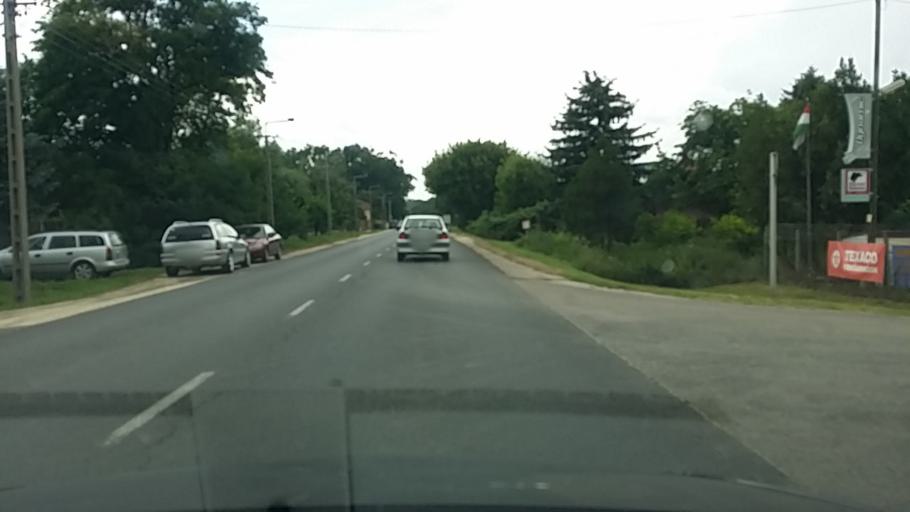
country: HU
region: Pest
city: Orkeny
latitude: 47.1228
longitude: 19.4361
